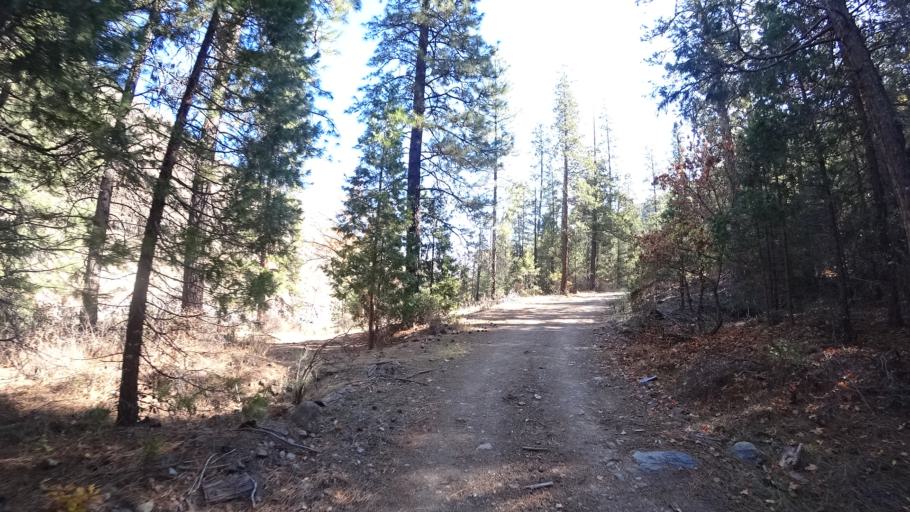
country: US
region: California
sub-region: Siskiyou County
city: Yreka
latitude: 41.8546
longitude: -122.7707
